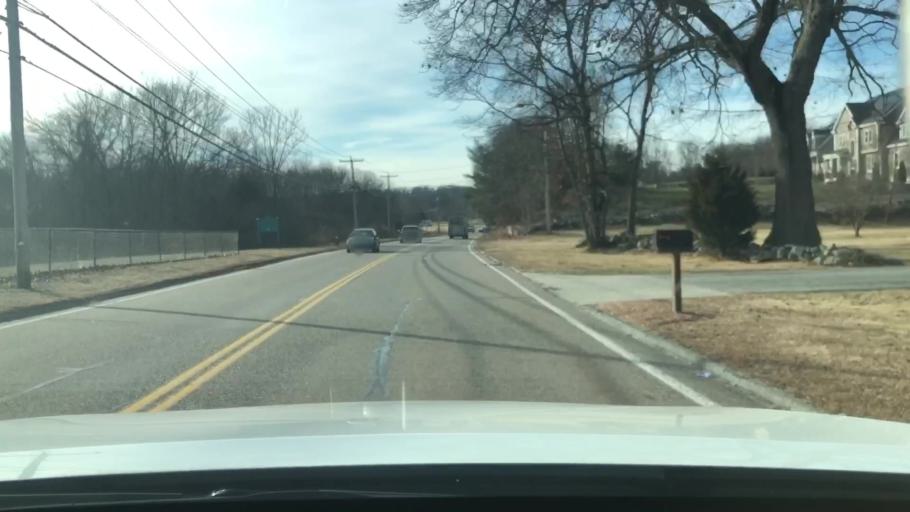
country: US
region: Massachusetts
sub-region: Worcester County
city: Grafton
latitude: 42.1986
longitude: -71.7128
